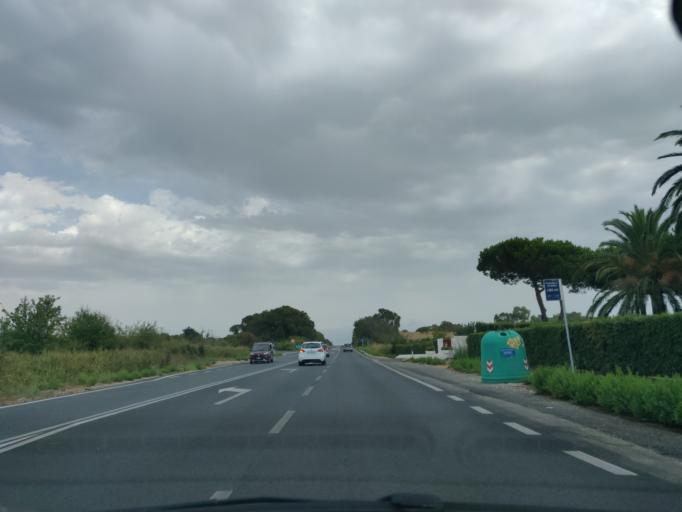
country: IT
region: Latium
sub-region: Citta metropolitana di Roma Capitale
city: Santa Marinella
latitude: 42.0320
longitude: 11.9341
